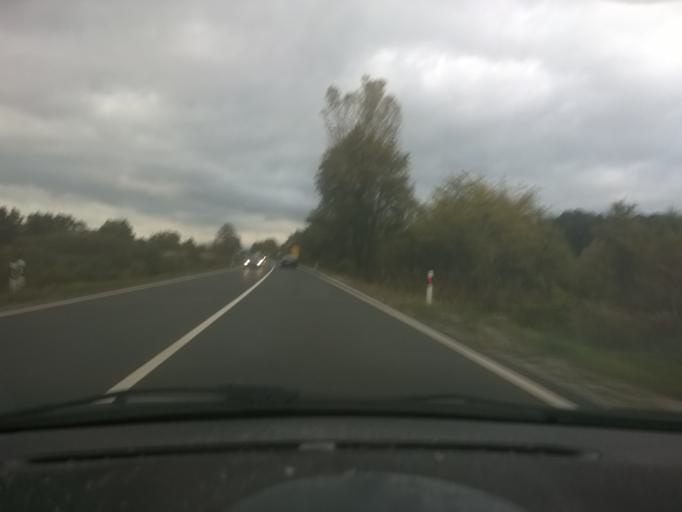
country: HR
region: Zagrebacka
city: Jakovlje
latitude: 45.9702
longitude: 15.8480
